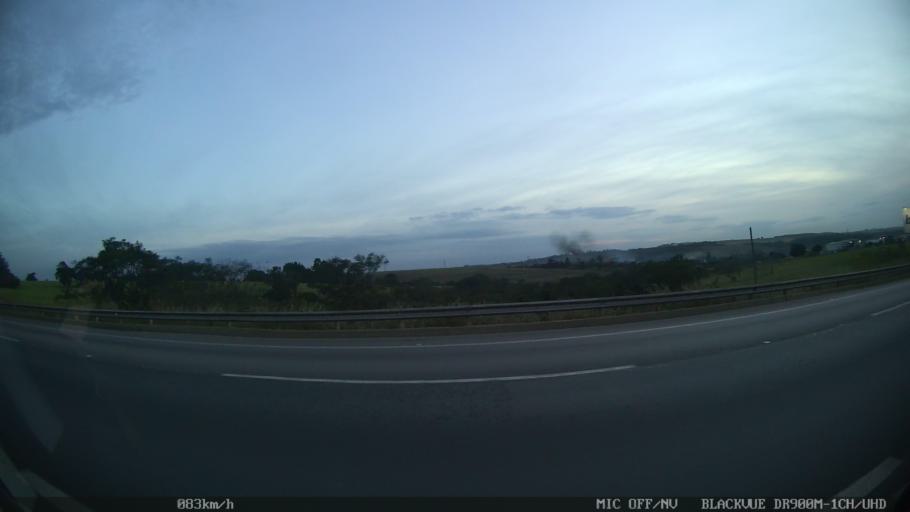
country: BR
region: Sao Paulo
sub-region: Limeira
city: Limeira
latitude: -22.6301
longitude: -47.3376
